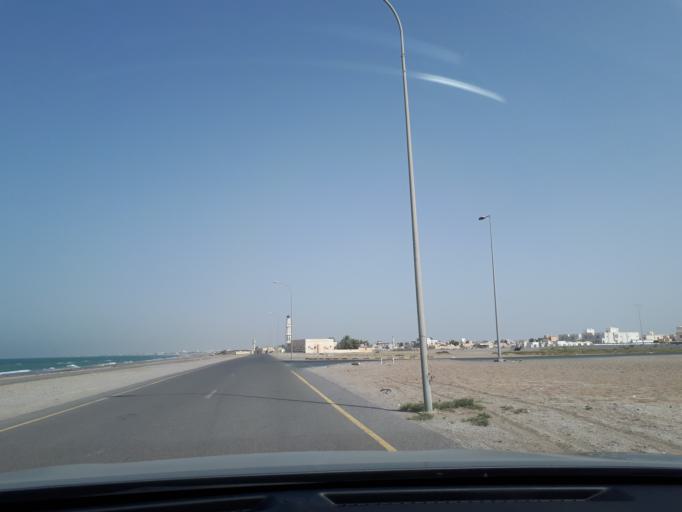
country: OM
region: Al Batinah
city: Barka'
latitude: 23.7226
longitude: 57.8512
